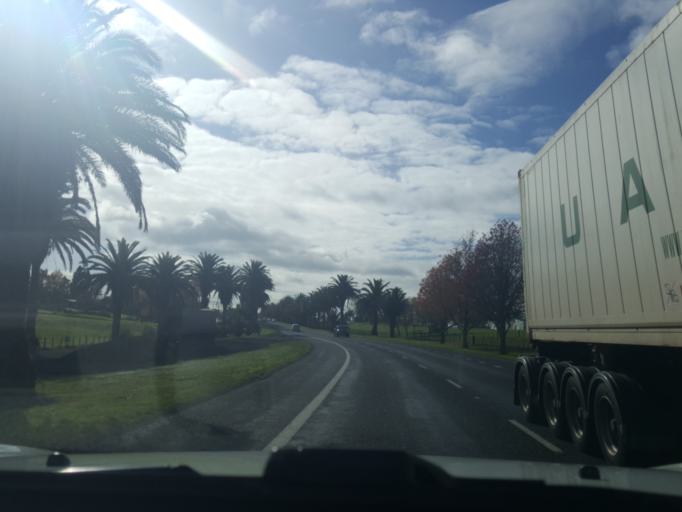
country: NZ
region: Waikato
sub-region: Hauraki District
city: Waihi
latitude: -37.4001
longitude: 175.8238
